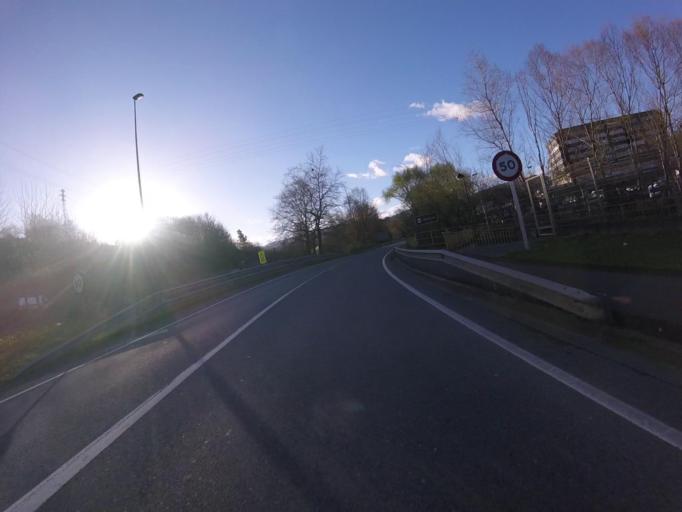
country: ES
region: Basque Country
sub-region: Provincia de Guipuzcoa
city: Errenteria
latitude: 43.3033
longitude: -1.8830
